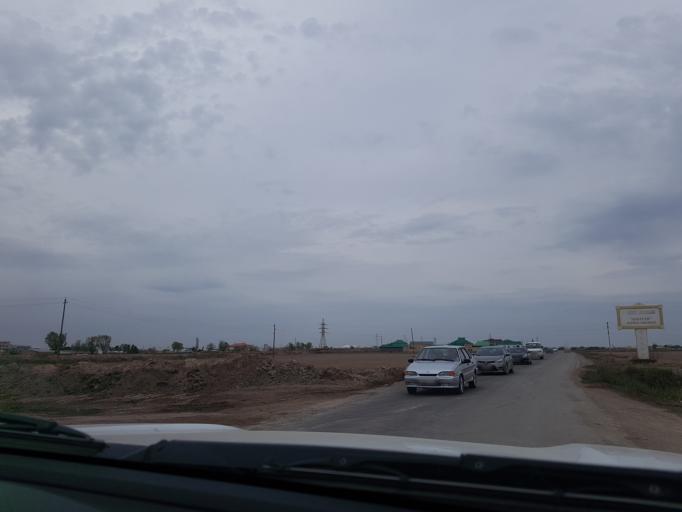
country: TM
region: Lebap
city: Turkmenabat
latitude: 39.0660
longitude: 63.5617
